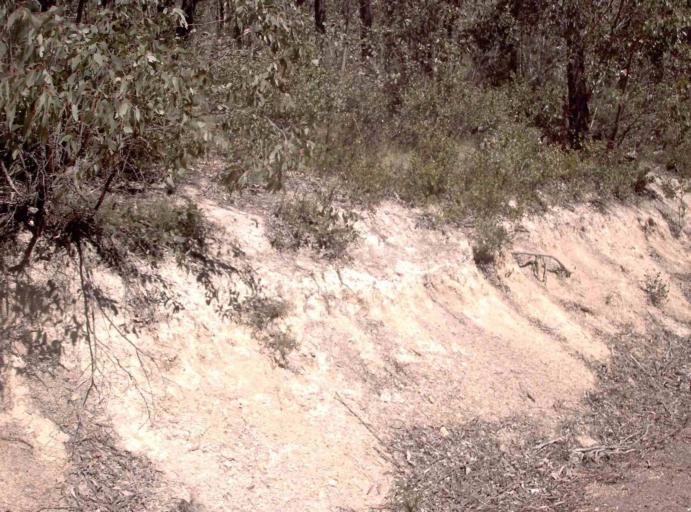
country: AU
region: New South Wales
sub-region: Snowy River
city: Jindabyne
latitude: -37.1072
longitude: 148.2504
